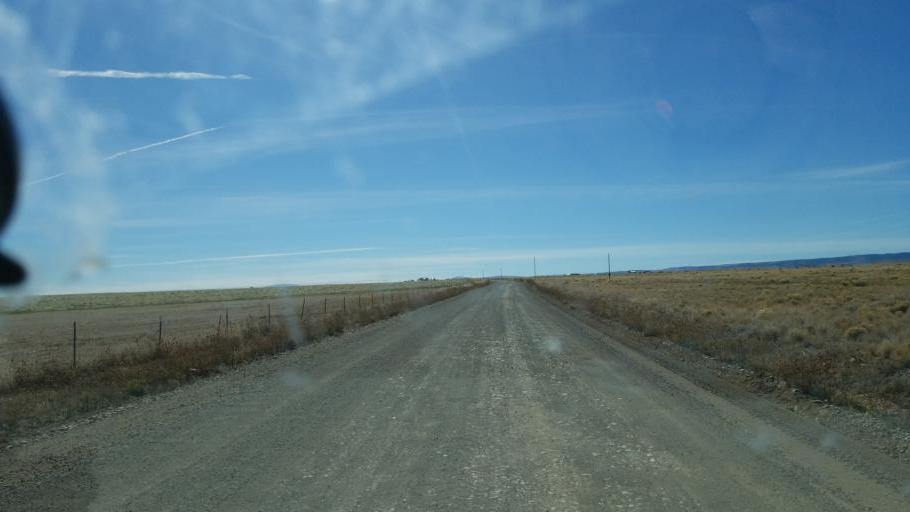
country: US
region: Colorado
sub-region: Rio Grande County
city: Monte Vista
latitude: 37.3995
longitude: -106.1490
